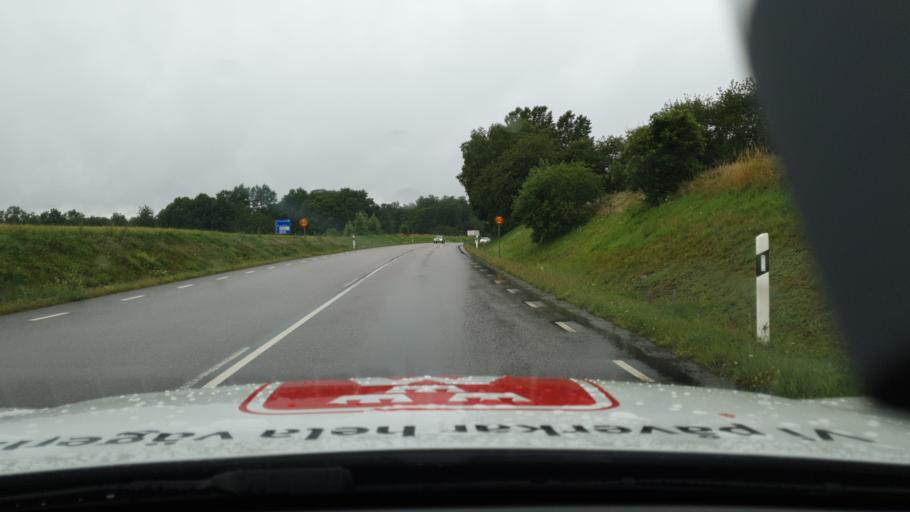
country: SE
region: Vaestra Goetaland
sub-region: Falkopings Kommun
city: Falkoeping
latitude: 58.1590
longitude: 13.4980
